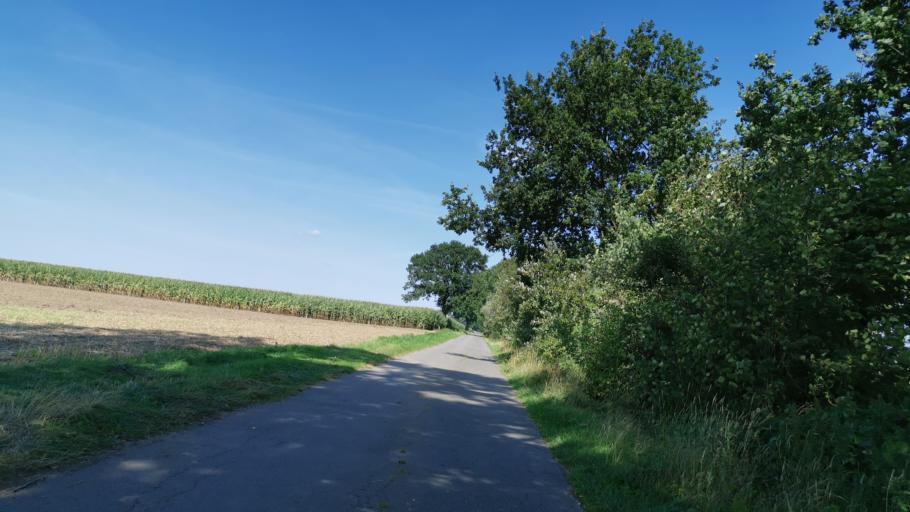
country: DE
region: Schleswig-Holstein
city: Gudow
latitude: 53.5660
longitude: 10.7701
